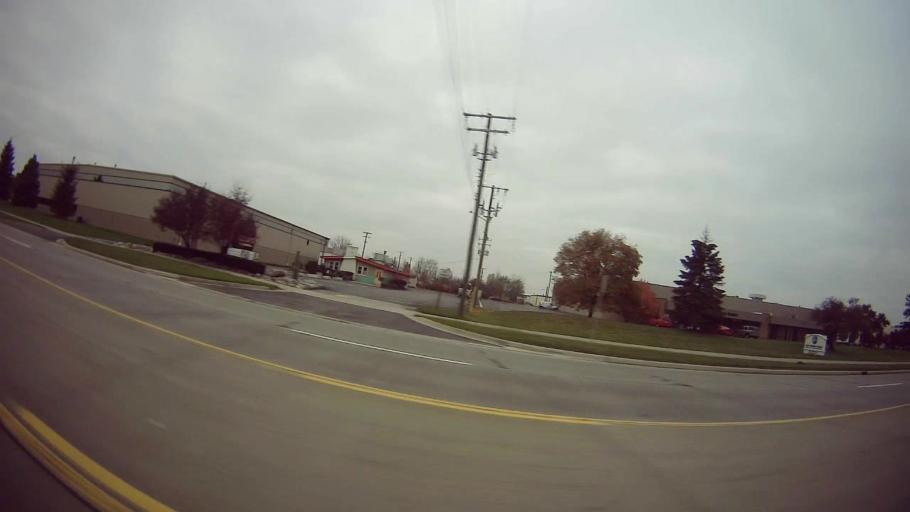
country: US
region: Michigan
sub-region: Oakland County
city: Madison Heights
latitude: 42.5384
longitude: -83.0871
